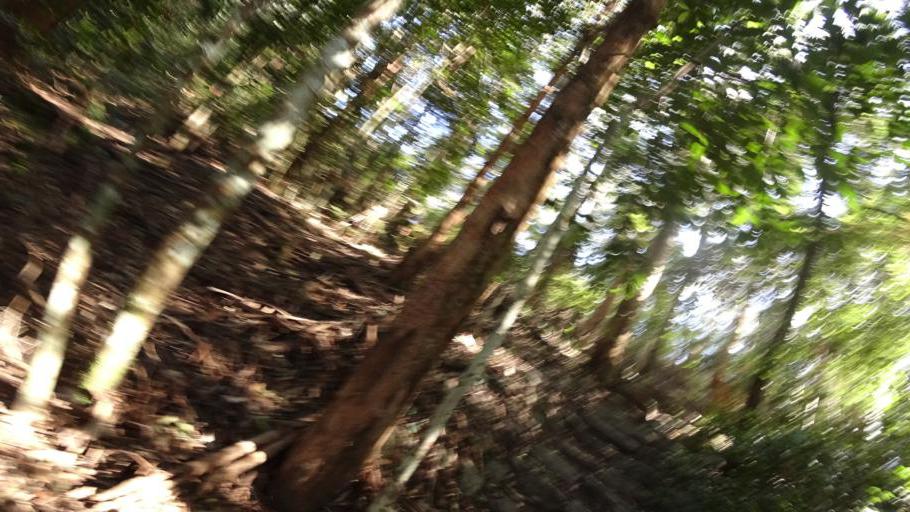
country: AU
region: Queensland
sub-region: Moreton Bay
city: Highvale
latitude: -27.3984
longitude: 152.7899
